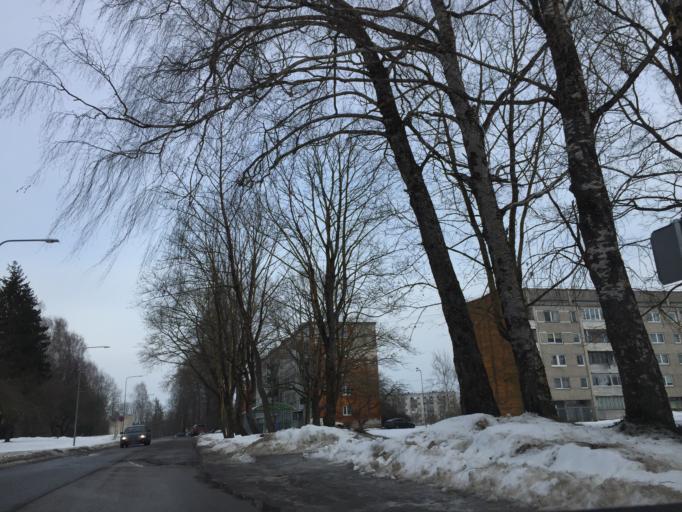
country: LV
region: Ikskile
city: Ikskile
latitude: 56.8449
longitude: 24.4337
